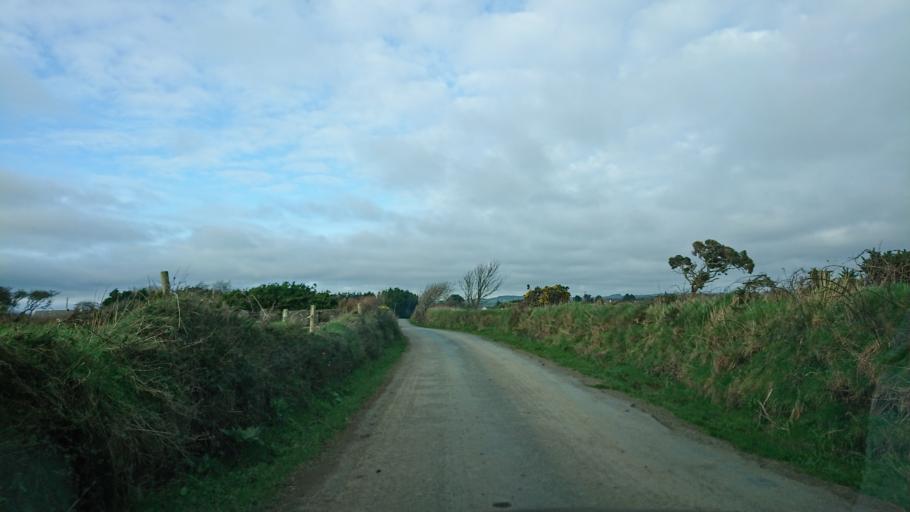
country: IE
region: Munster
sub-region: Waterford
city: Portlaw
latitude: 52.1454
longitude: -7.3056
